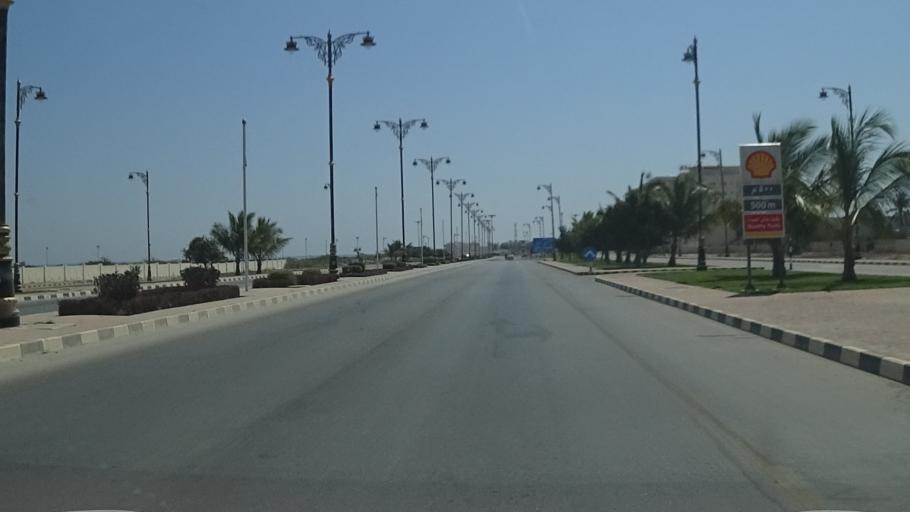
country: OM
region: Zufar
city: Salalah
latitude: 17.0308
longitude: 54.1723
